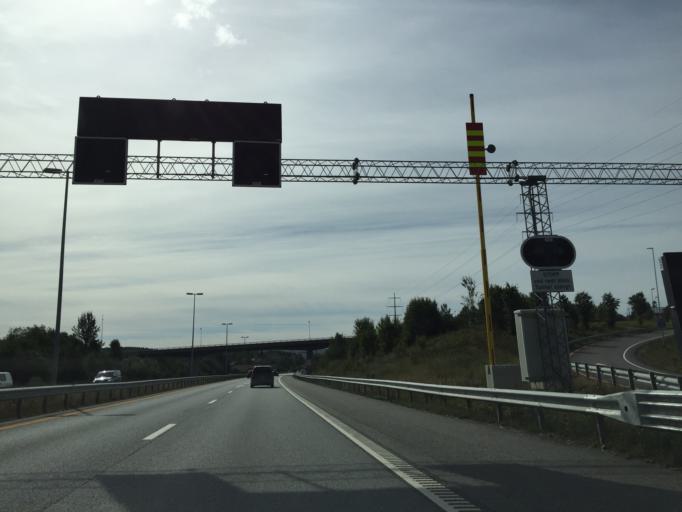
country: NO
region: Akershus
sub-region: Vestby
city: Vestby
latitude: 59.6045
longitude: 10.7366
